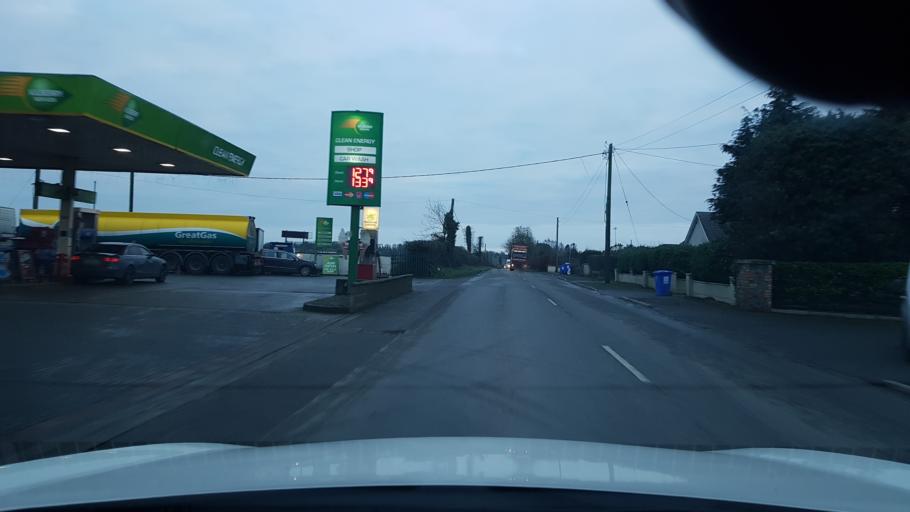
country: IE
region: Leinster
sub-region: An Mhi
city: Navan
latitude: 53.7013
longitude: -6.6812
